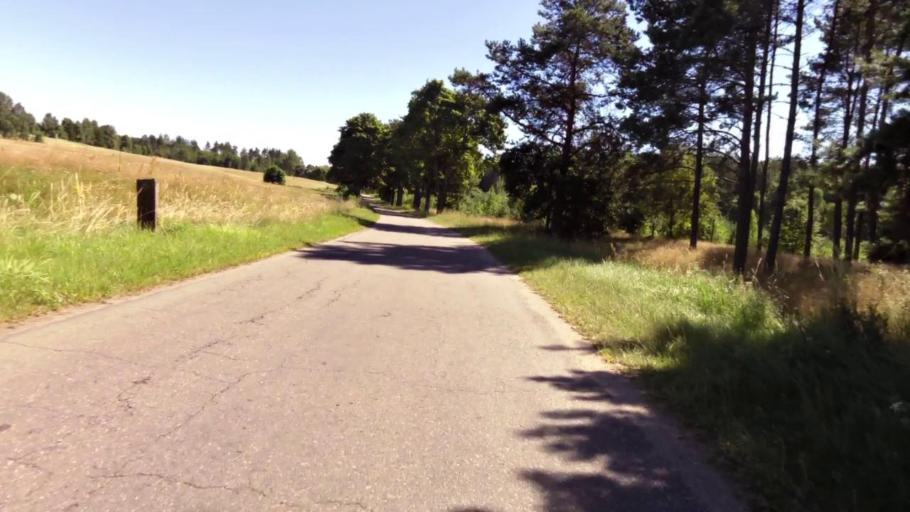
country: PL
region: West Pomeranian Voivodeship
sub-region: Powiat szczecinecki
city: Bialy Bor
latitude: 53.9490
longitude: 16.8460
